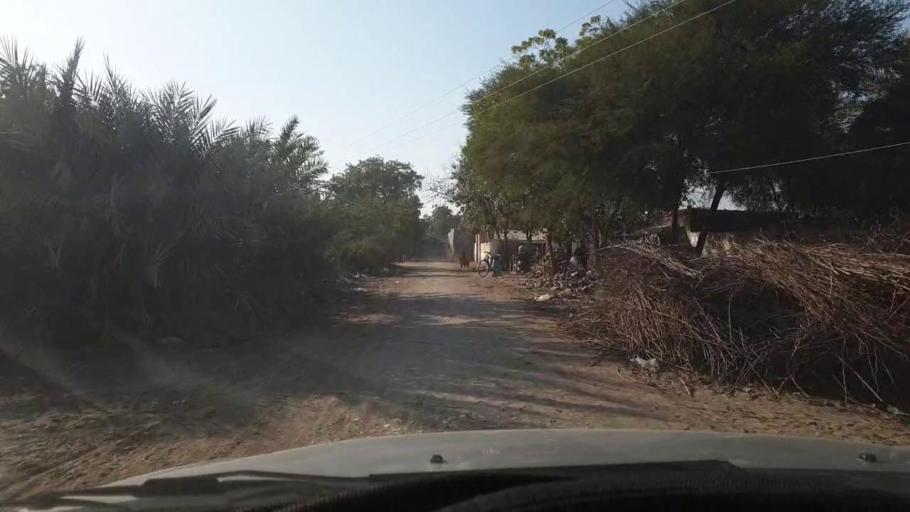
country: PK
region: Sindh
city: Mirpur Mathelo
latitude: 28.0353
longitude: 69.5934
